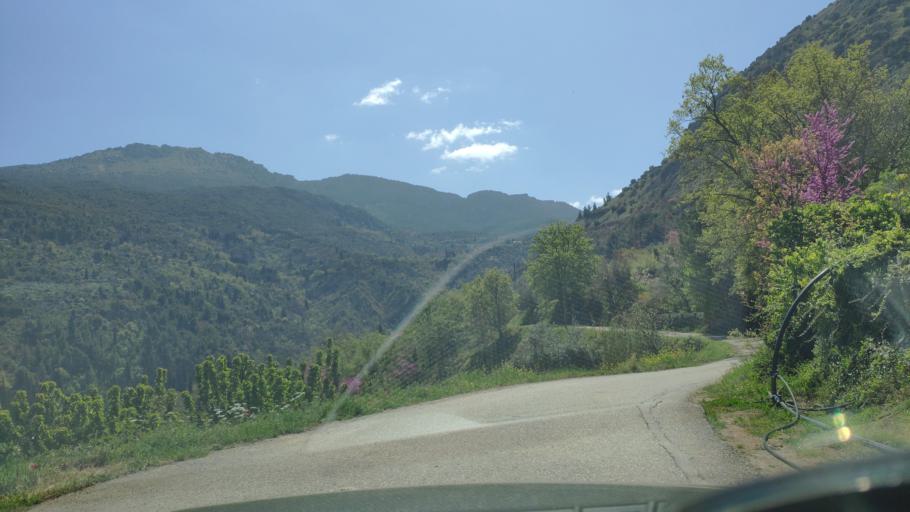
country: GR
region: West Greece
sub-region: Nomos Achaias
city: Aiyira
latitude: 38.0683
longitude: 22.3364
